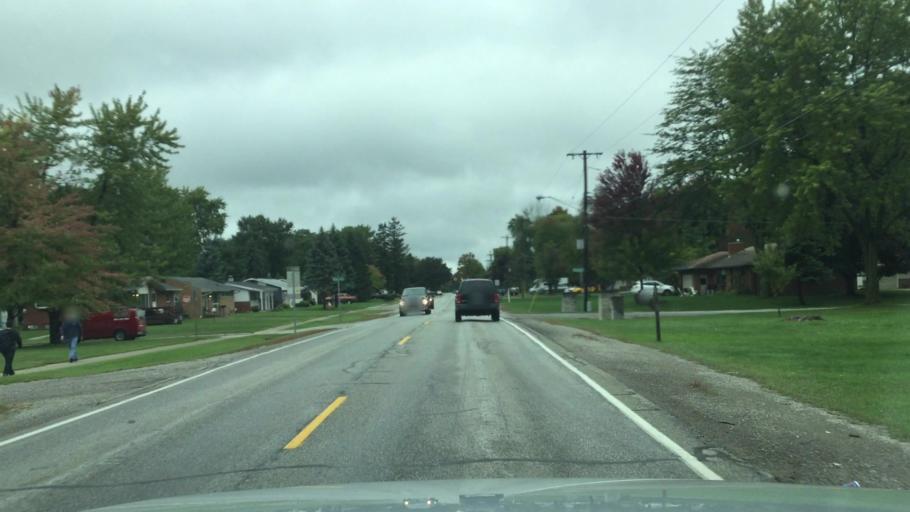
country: US
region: Michigan
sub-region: Saginaw County
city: Shields
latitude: 43.4440
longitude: -84.0099
